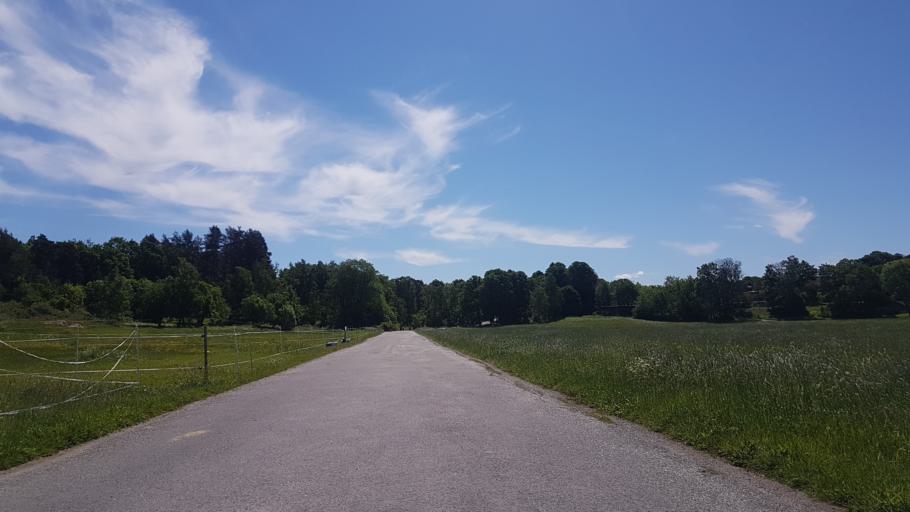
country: SE
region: Stockholm
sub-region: Lidingo
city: Lidingoe
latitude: 59.3353
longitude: 18.1204
